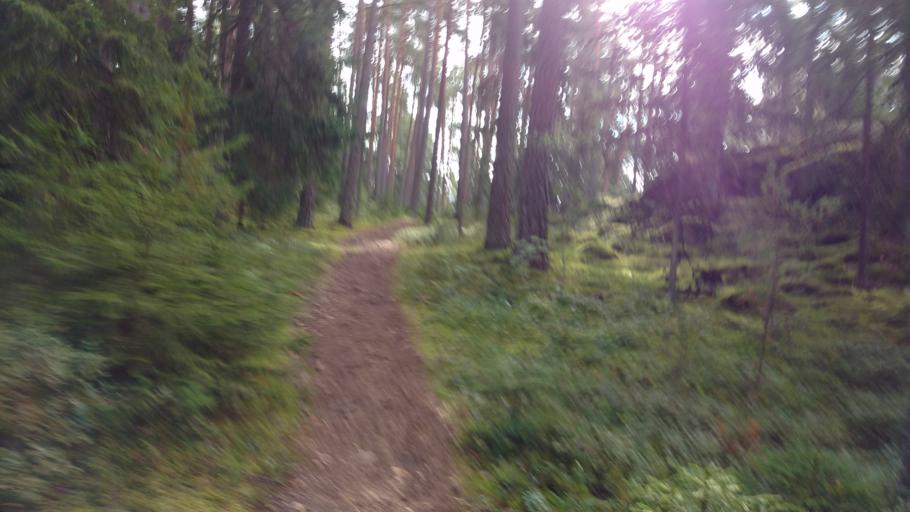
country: FI
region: Varsinais-Suomi
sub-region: Salo
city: Salo
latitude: 60.3654
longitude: 23.1835
